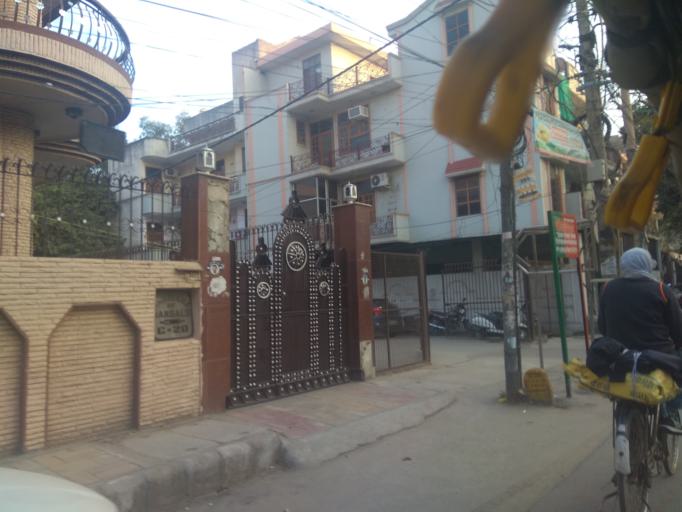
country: IN
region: NCT
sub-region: West Delhi
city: Nangloi Jat
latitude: 28.6305
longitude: 77.0764
